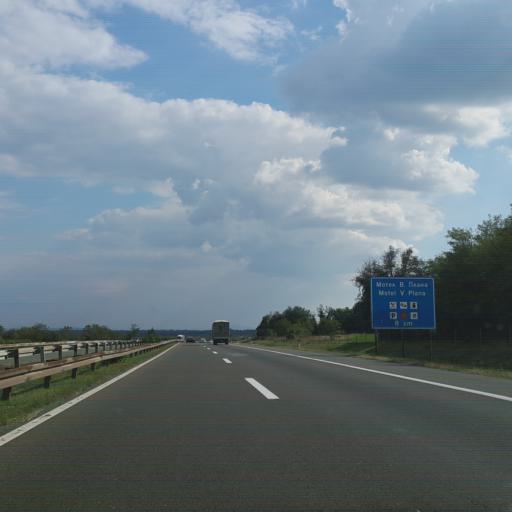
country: RS
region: Central Serbia
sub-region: Podunavski Okrug
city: Velika Plana
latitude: 44.4077
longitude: 21.0582
